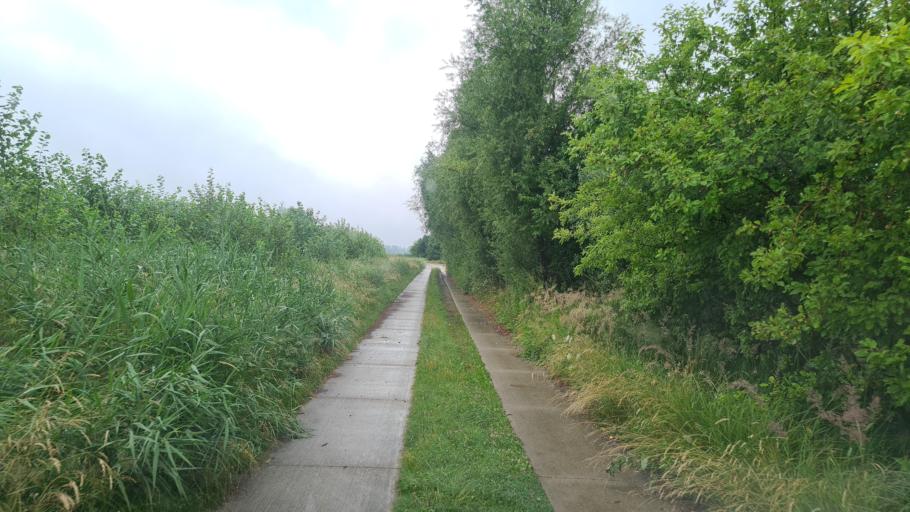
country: DE
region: Brandenburg
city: Trebbin
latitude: 52.1847
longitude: 13.2566
